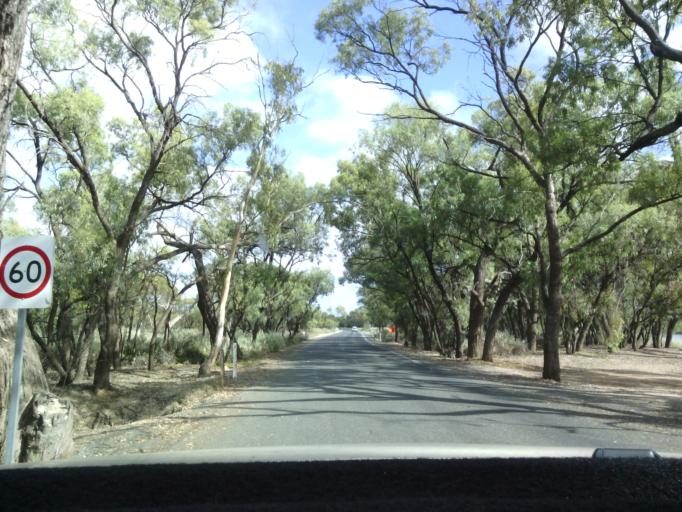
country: AU
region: South Australia
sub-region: Berri and Barmera
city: Berri
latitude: -34.2858
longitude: 140.6313
